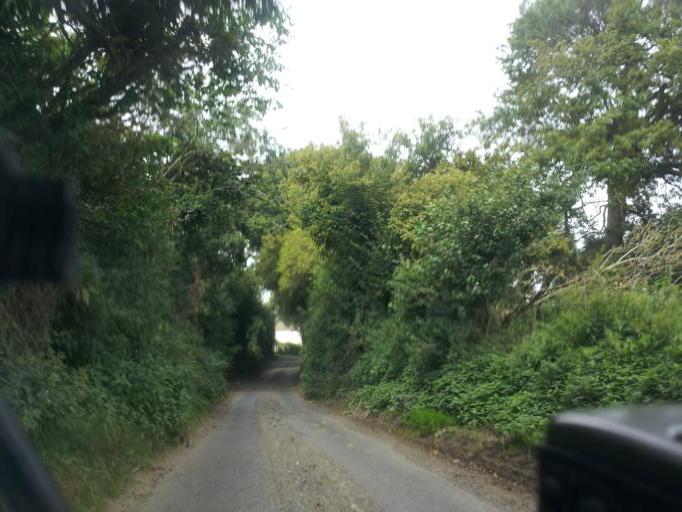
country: GB
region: England
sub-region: Kent
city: Newington
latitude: 51.3622
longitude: 0.6624
